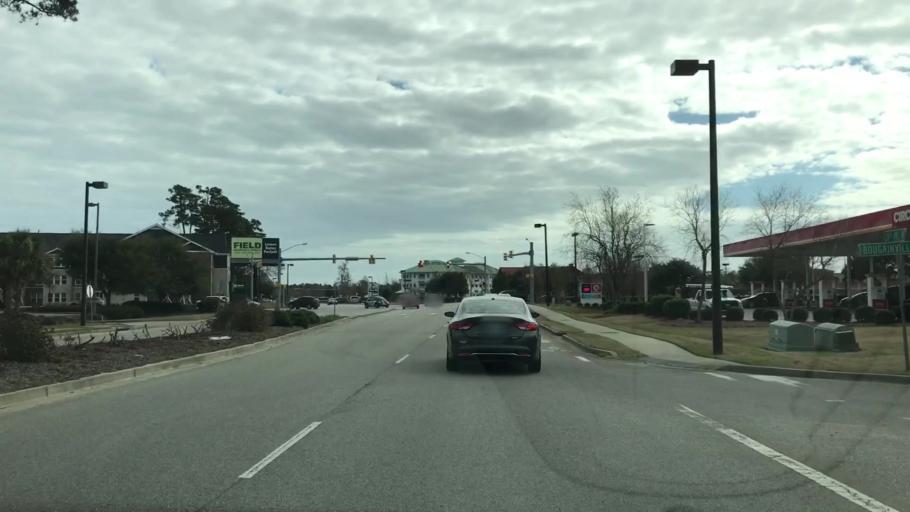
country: US
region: South Carolina
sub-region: Horry County
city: Myrtle Beach
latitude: 33.7274
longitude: -78.8692
